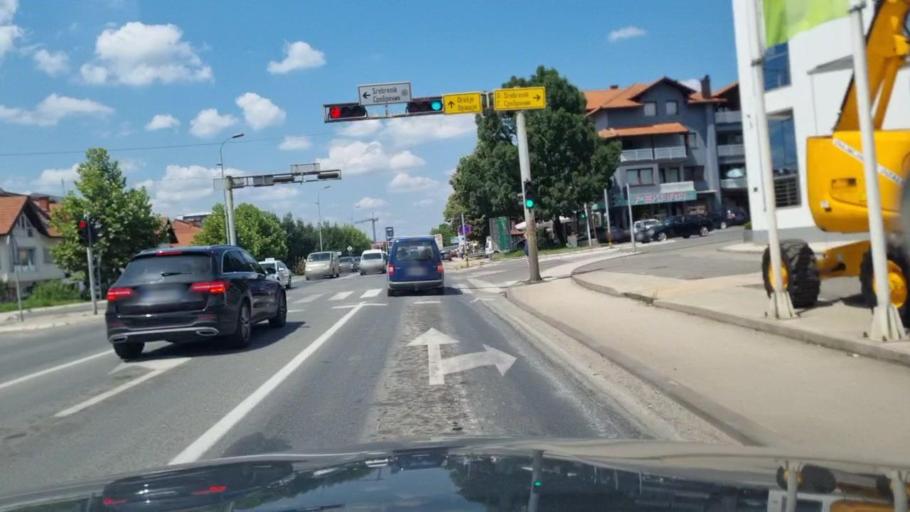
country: BA
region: Federation of Bosnia and Herzegovina
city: Srebrenik
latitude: 44.7045
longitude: 18.4939
